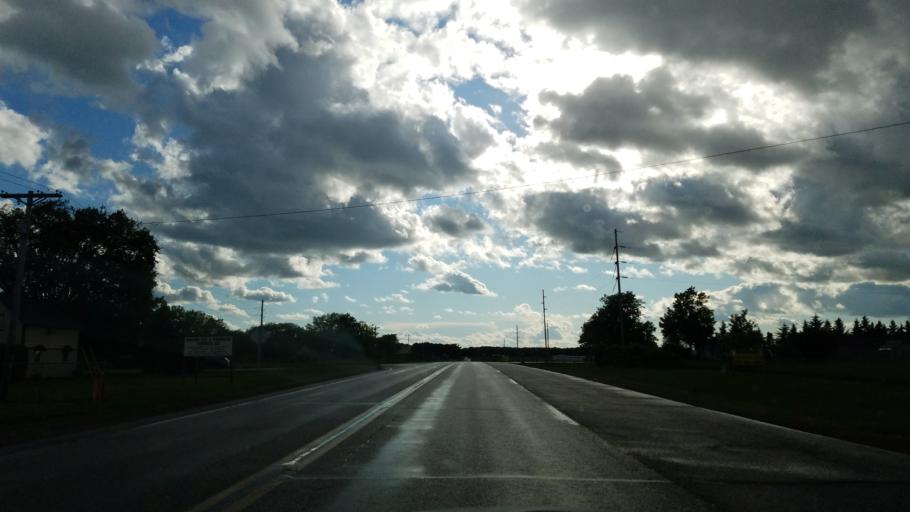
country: US
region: Wisconsin
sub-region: Polk County
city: Osceola
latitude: 45.3432
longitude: -92.6504
